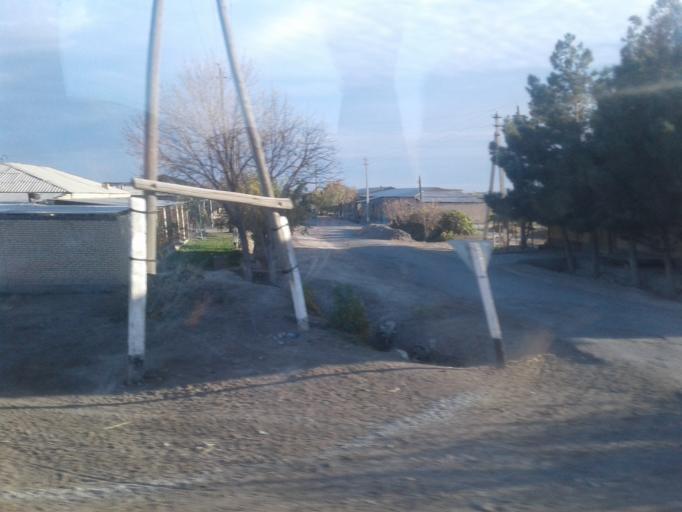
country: TM
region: Mary
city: Seydi
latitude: 39.3662
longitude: 62.9378
